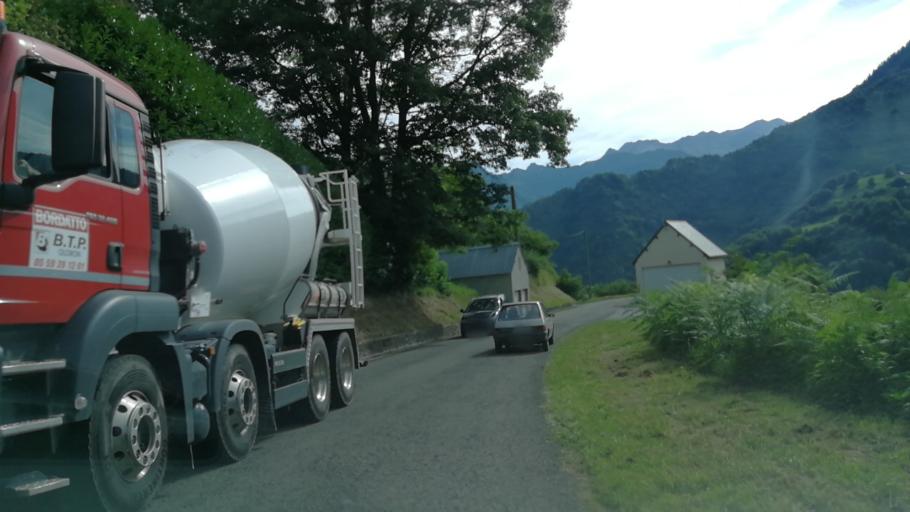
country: FR
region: Aquitaine
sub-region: Departement des Pyrenees-Atlantiques
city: Arette
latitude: 42.9331
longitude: -0.6324
